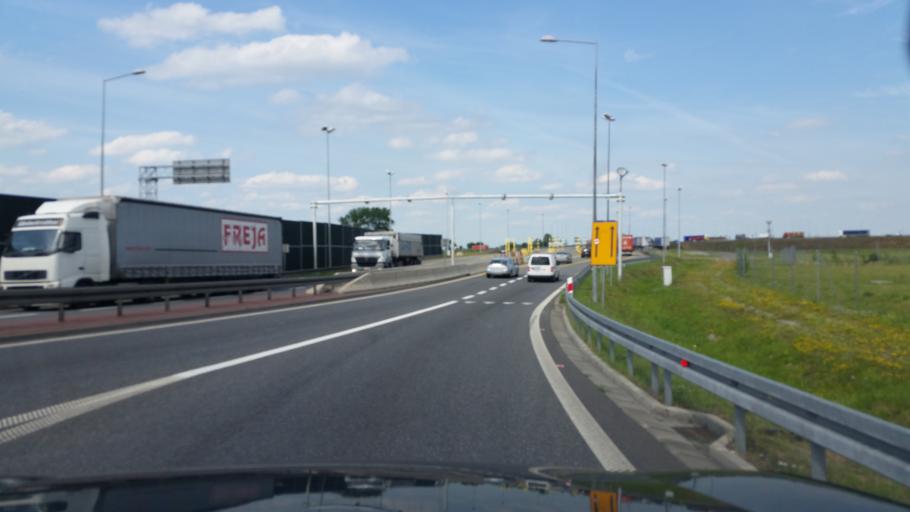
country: PL
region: Masovian Voivodeship
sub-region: Powiat zyrardowski
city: Wiskitki
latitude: 52.0884
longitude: 20.3578
